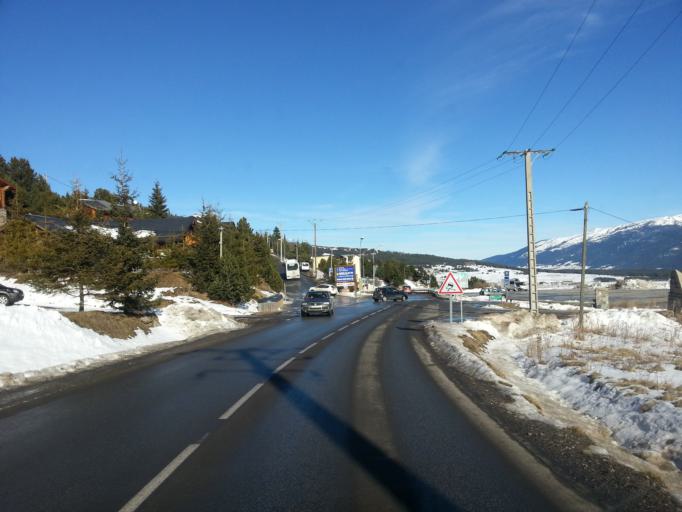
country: ES
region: Catalonia
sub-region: Provincia de Girona
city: Llivia
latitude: 42.5671
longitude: 2.0725
